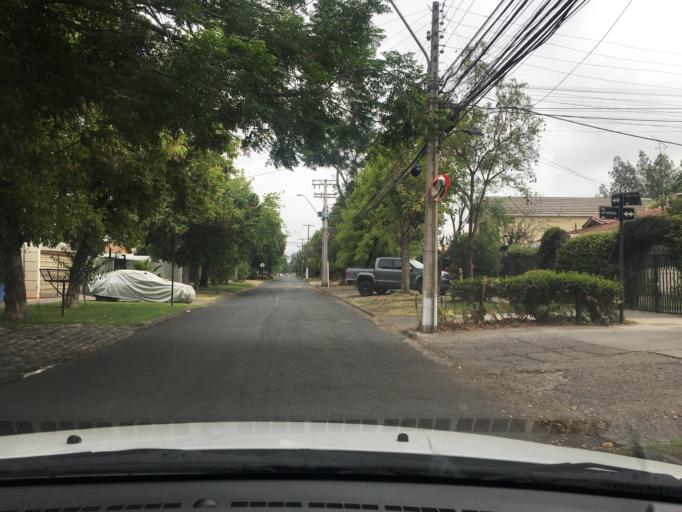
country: CL
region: Santiago Metropolitan
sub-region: Provincia de Santiago
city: Villa Presidente Frei, Nunoa, Santiago, Chile
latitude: -33.4565
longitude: -70.5547
